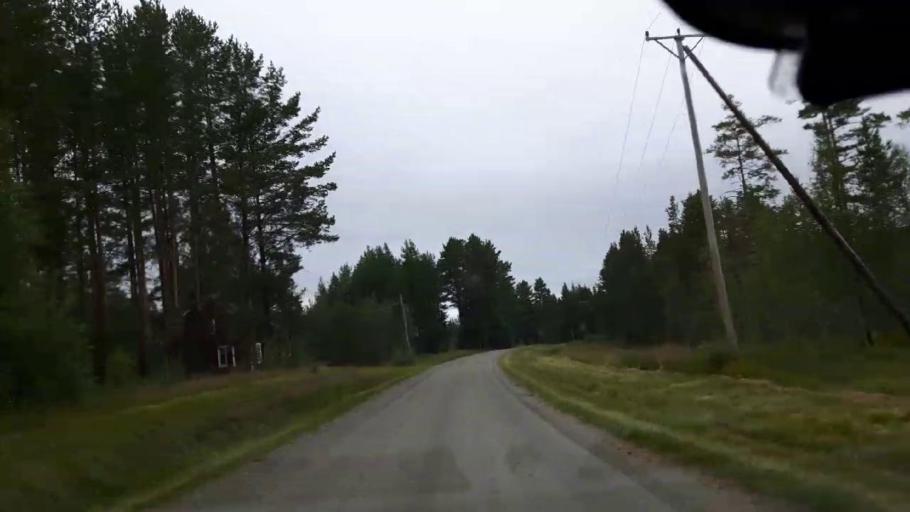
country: SE
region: Vaesternorrland
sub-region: Ange Kommun
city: Fransta
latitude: 62.7969
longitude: 16.0277
